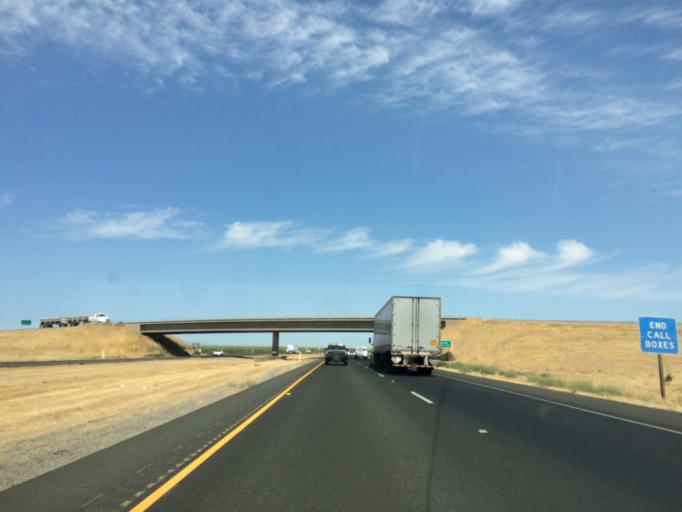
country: US
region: California
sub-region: Yolo County
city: Dunnigan
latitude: 38.9245
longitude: -121.9994
